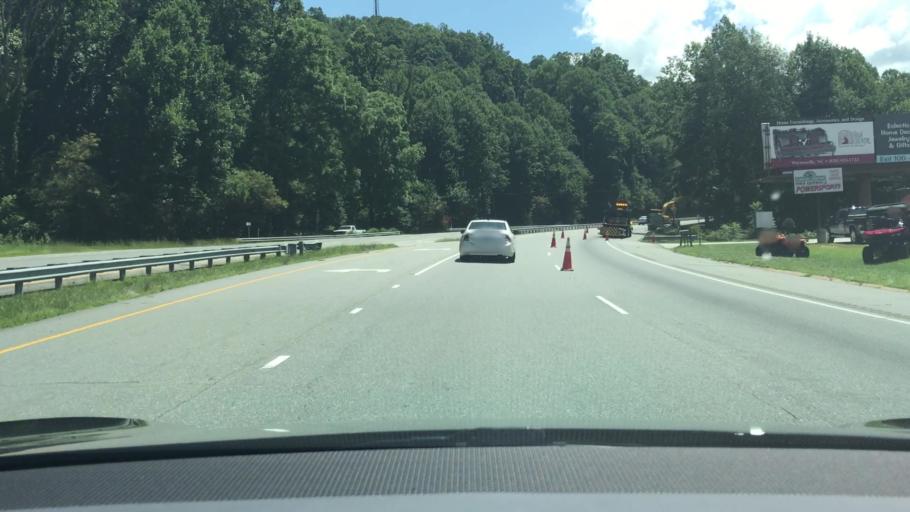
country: US
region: North Carolina
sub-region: Jackson County
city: Sylva
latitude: 35.3942
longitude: -83.1677
